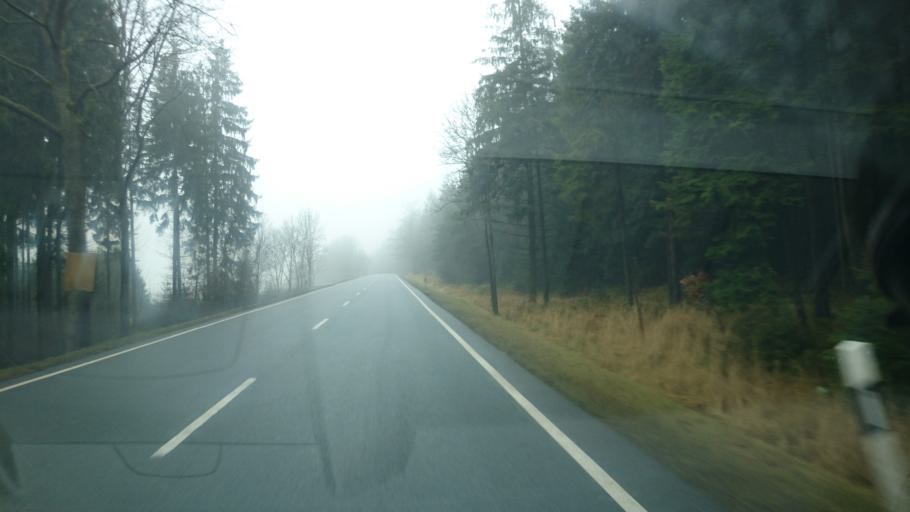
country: DE
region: Thuringia
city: Tanna
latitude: 50.4784
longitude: 11.8383
